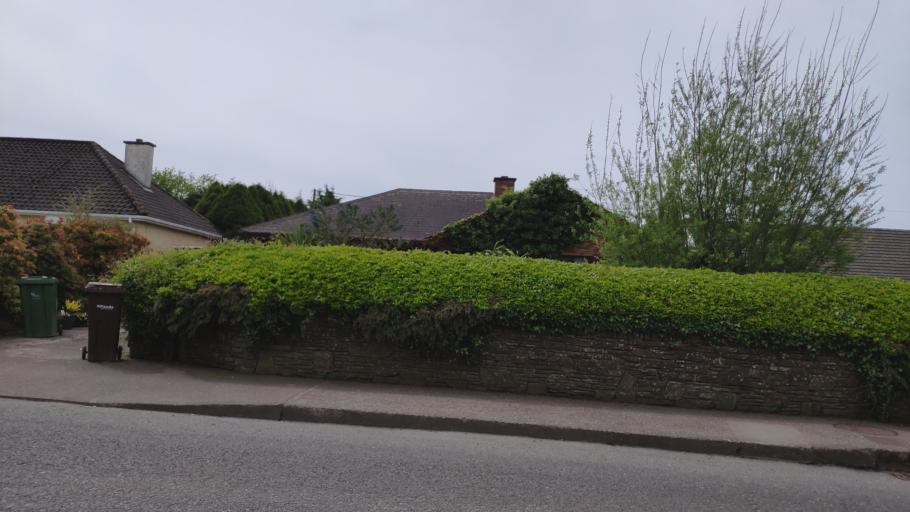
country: IE
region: Munster
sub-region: County Cork
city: Cork
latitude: 51.9192
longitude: -8.4516
